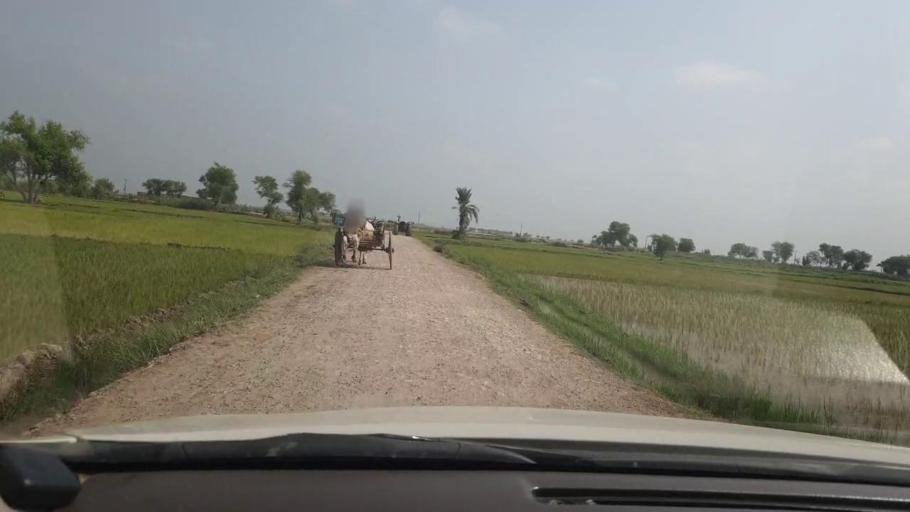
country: PK
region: Sindh
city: Shikarpur
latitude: 28.0132
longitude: 68.5943
